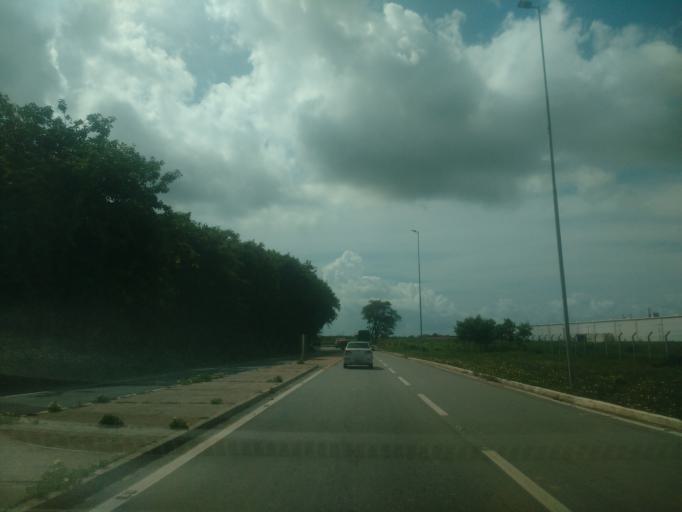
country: BR
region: Alagoas
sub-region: Marechal Deodoro
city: Marechal Deodoro
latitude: -9.6853
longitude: -35.8264
